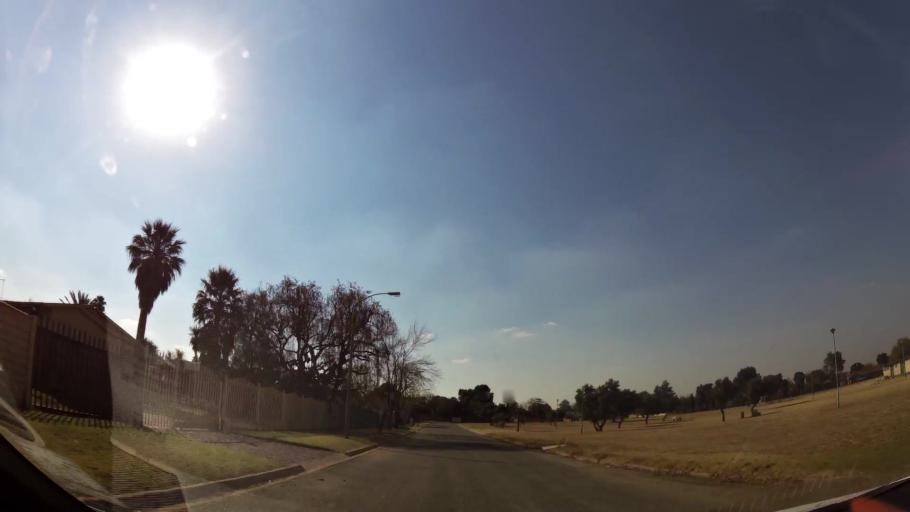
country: ZA
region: Gauteng
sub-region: Ekurhuleni Metropolitan Municipality
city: Boksburg
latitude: -26.2452
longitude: 28.2952
